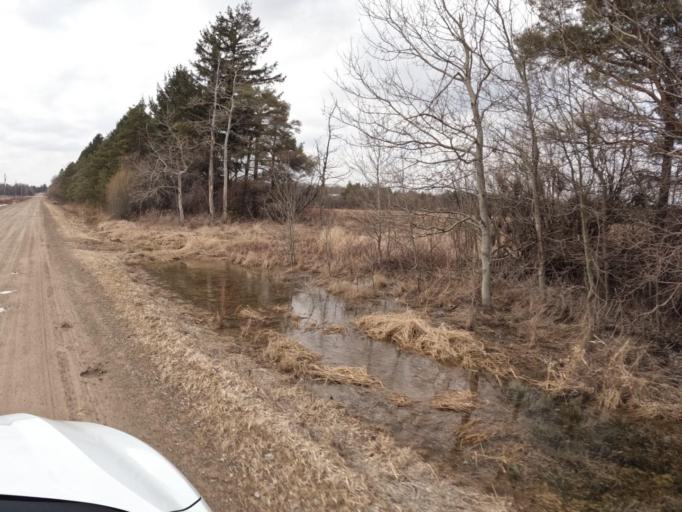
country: CA
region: Ontario
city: Shelburne
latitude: 44.0356
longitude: -80.2233
